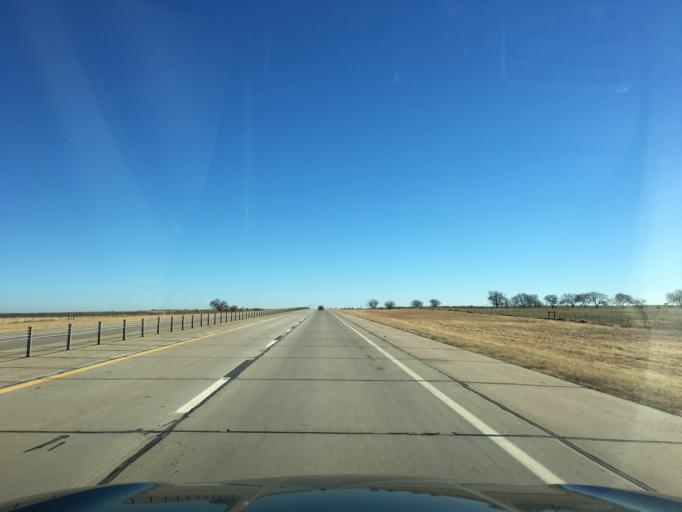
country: US
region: Oklahoma
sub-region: Noble County
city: Perry
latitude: 36.4005
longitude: -97.2442
